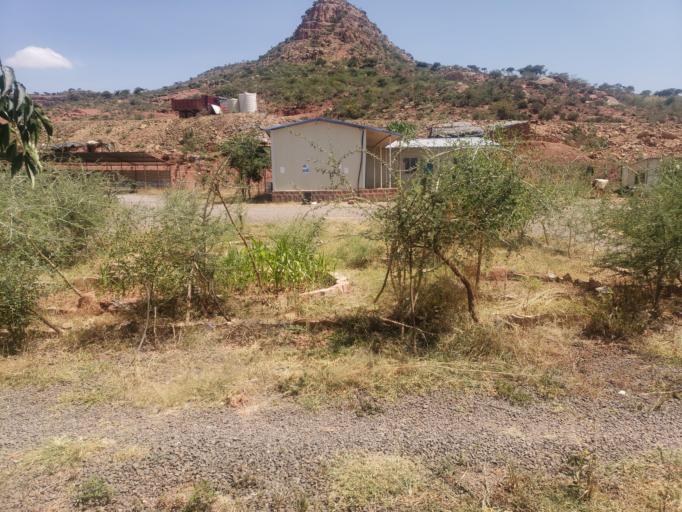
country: ET
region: Tigray
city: Aksum
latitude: 13.5320
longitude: 38.5702
